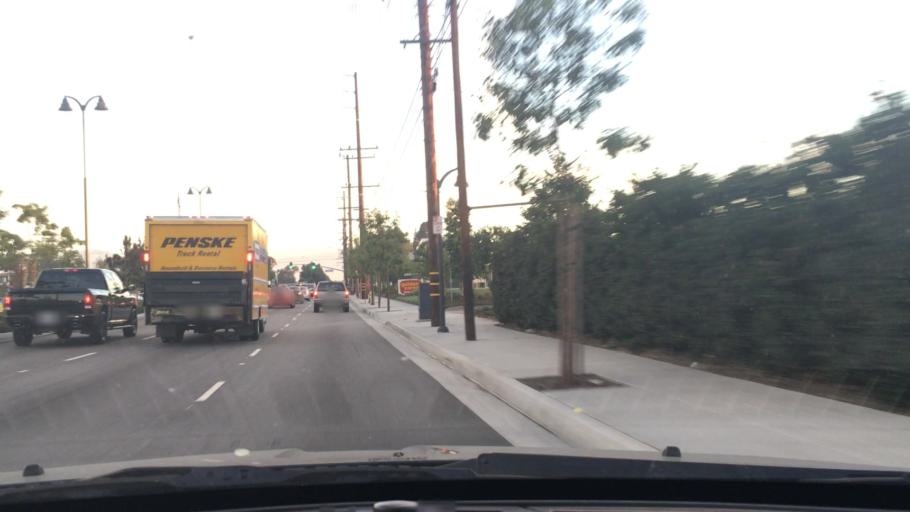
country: US
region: California
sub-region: Los Angeles County
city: Downey
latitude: 33.9528
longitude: -118.1143
